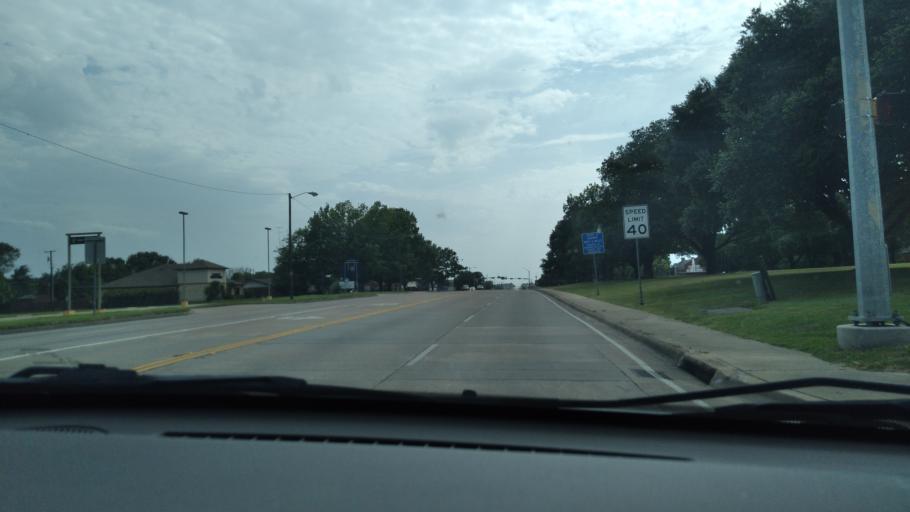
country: US
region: Texas
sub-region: Navarro County
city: Corsicana
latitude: 32.0756
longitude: -96.4965
